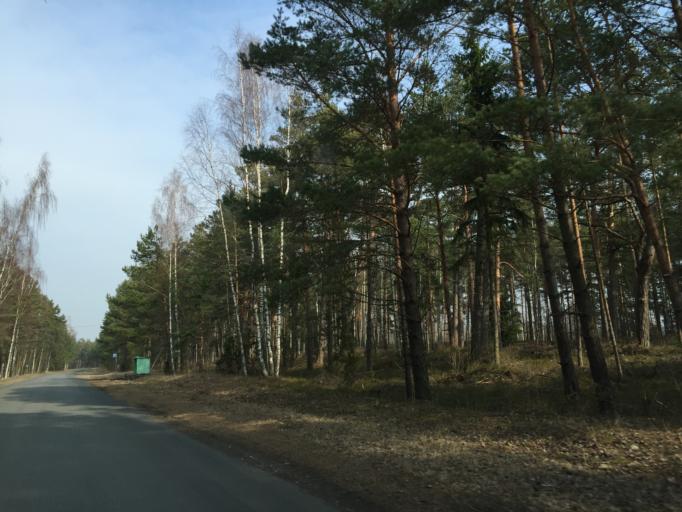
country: LV
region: Salacgrivas
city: Ainazi
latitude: 57.9031
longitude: 24.3777
